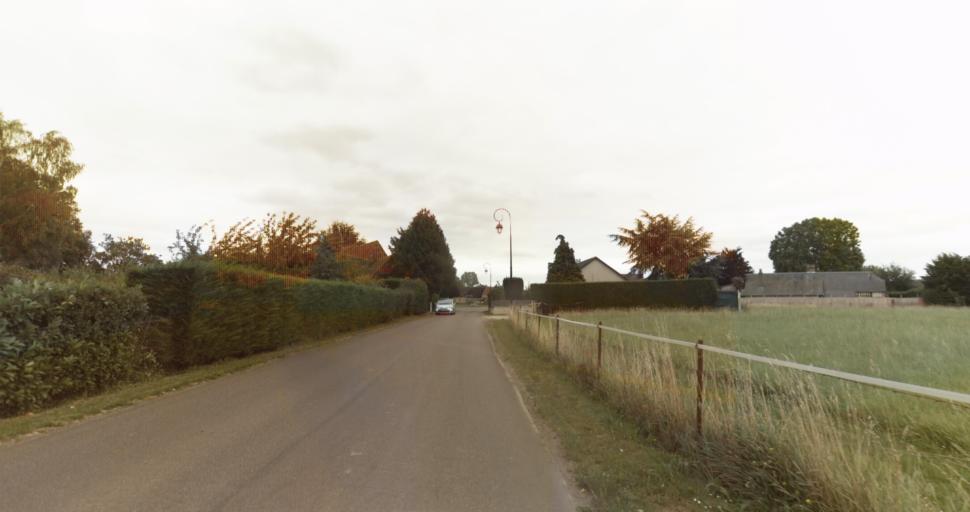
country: FR
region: Haute-Normandie
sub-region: Departement de l'Eure
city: Gravigny
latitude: 49.0046
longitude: 1.2331
